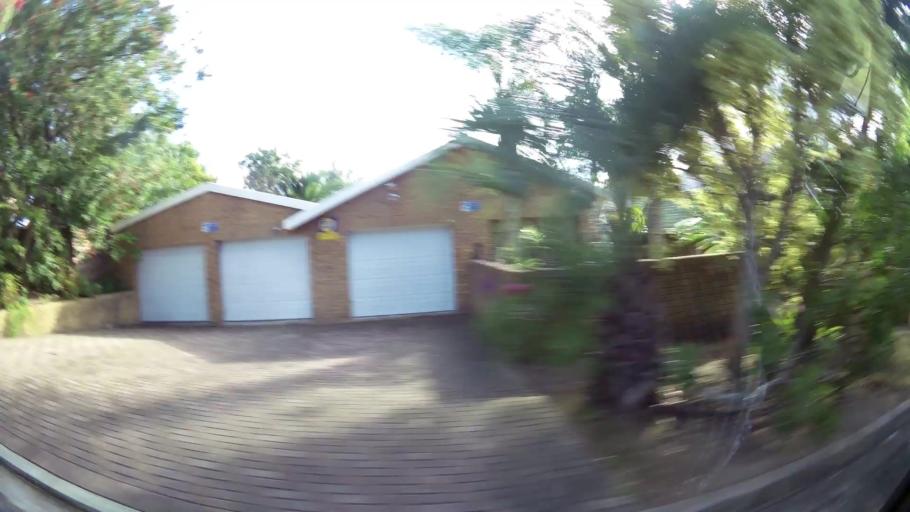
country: ZA
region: Western Cape
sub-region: Eden District Municipality
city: George
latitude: -33.9586
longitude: 22.4923
